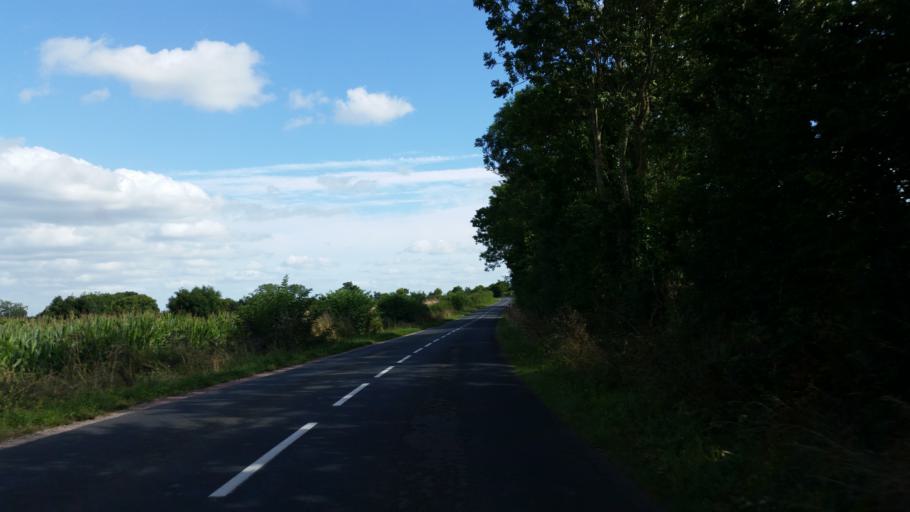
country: FR
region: Lower Normandy
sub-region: Departement de la Manche
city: Sainte-Mere-Eglise
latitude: 49.4522
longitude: -1.2658
